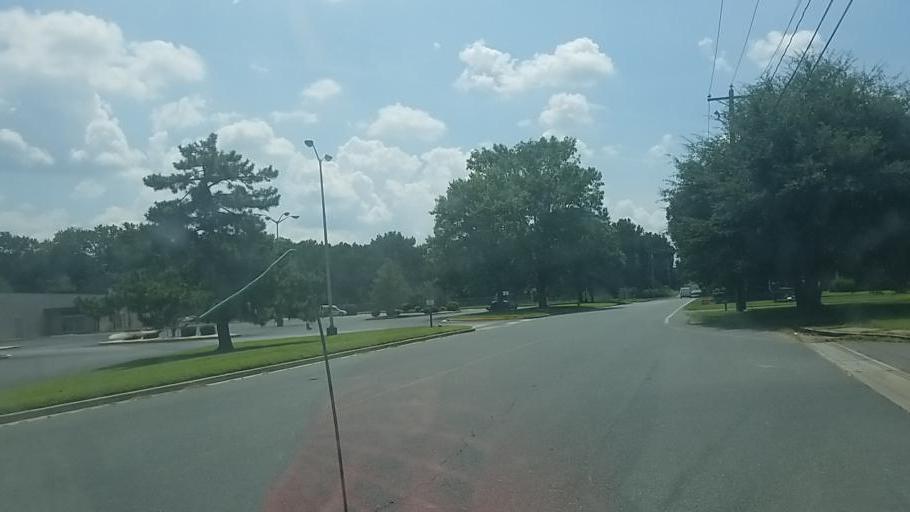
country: US
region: Maryland
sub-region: Wicomico County
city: Salisbury
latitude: 38.3643
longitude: -75.5479
